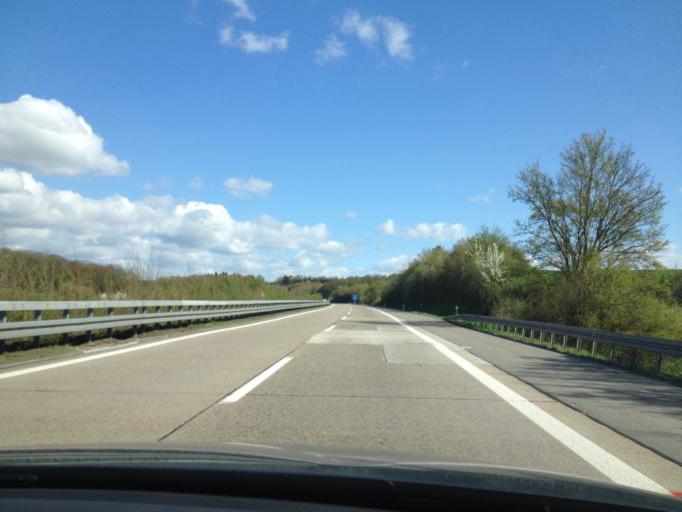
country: DE
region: Baden-Wuerttemberg
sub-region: Regierungsbezirk Stuttgart
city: Neuenstadt am Kocher
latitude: 49.2549
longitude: 9.3529
